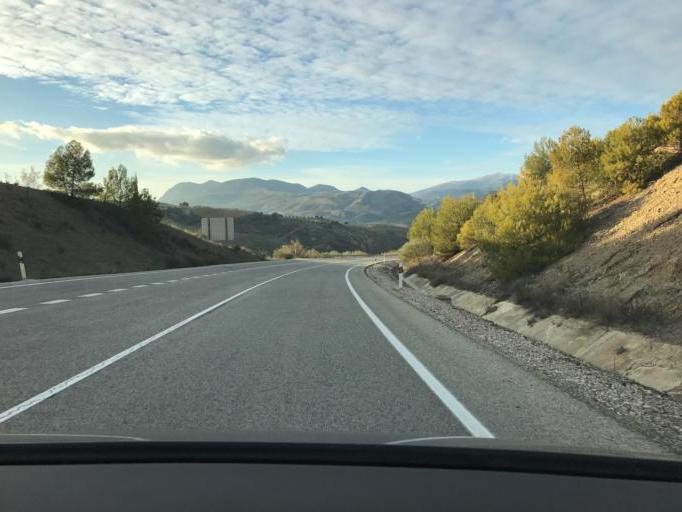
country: ES
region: Andalusia
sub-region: Provincia de Jaen
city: Huelma
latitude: 37.6343
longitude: -3.4079
